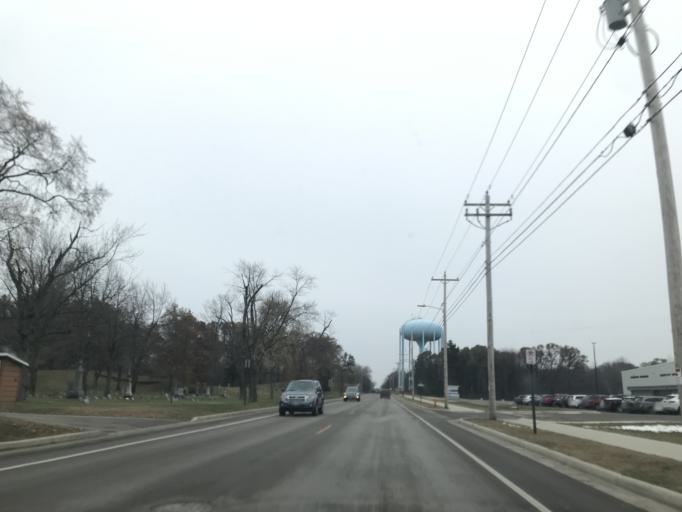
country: US
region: Wisconsin
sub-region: Marinette County
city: Marinette
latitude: 45.0809
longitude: -87.6296
